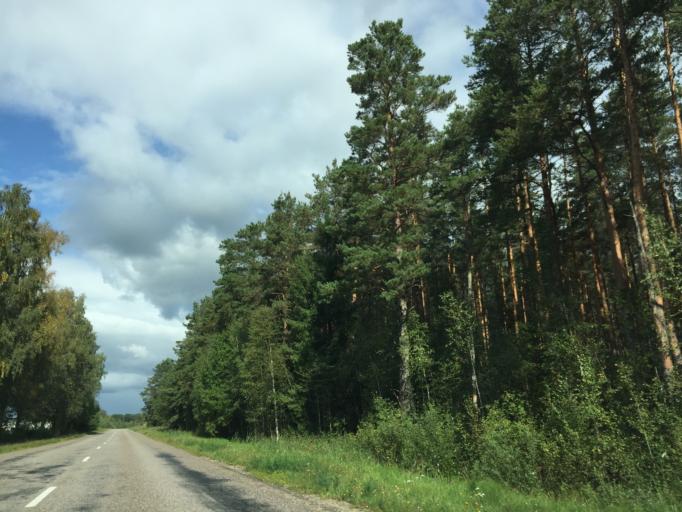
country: LV
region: Pargaujas
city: Stalbe
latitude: 57.4482
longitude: 24.9219
